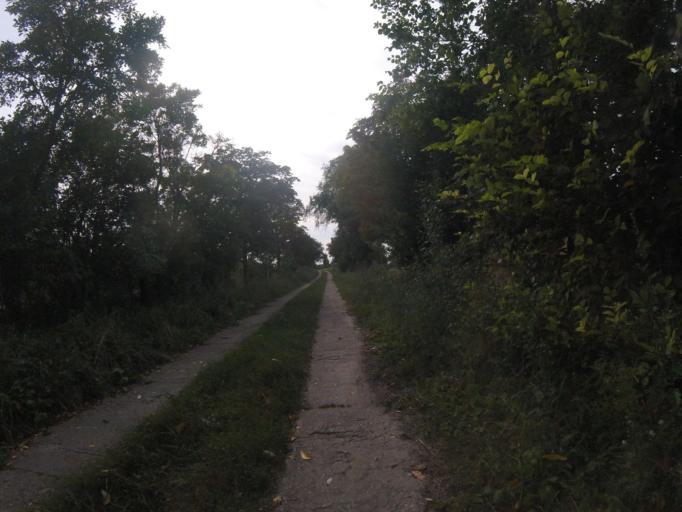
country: DE
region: Brandenburg
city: Mittenwalde
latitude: 52.2802
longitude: 13.4960
